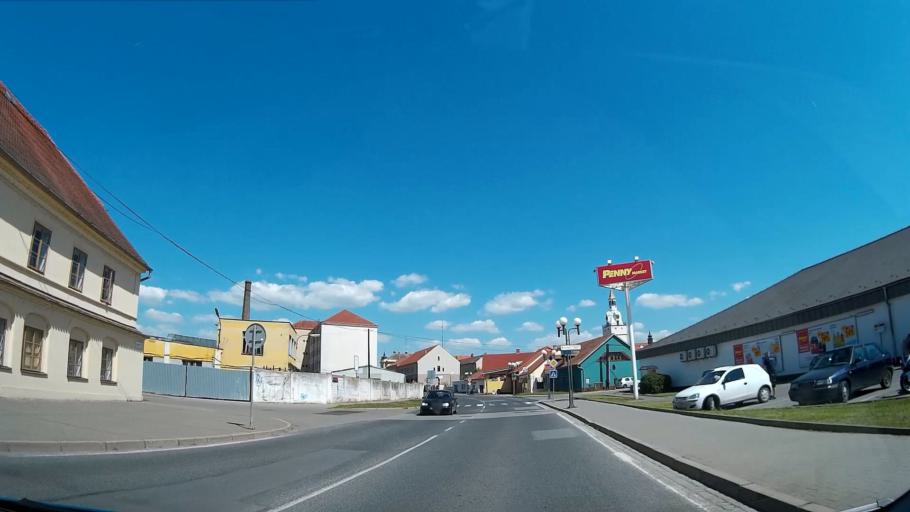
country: CZ
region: South Moravian
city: Ivancice
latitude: 49.0996
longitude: 16.3756
